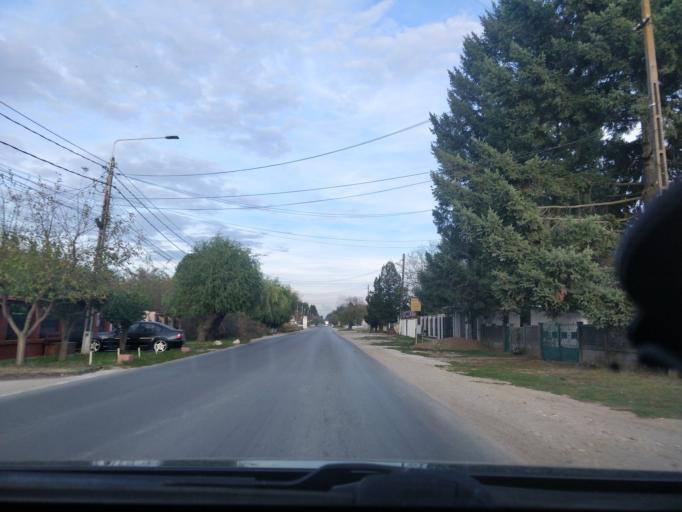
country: RO
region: Giurgiu
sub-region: Comuna Bolintin Vale
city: Bolintin Vale
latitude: 44.4434
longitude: 25.7415
